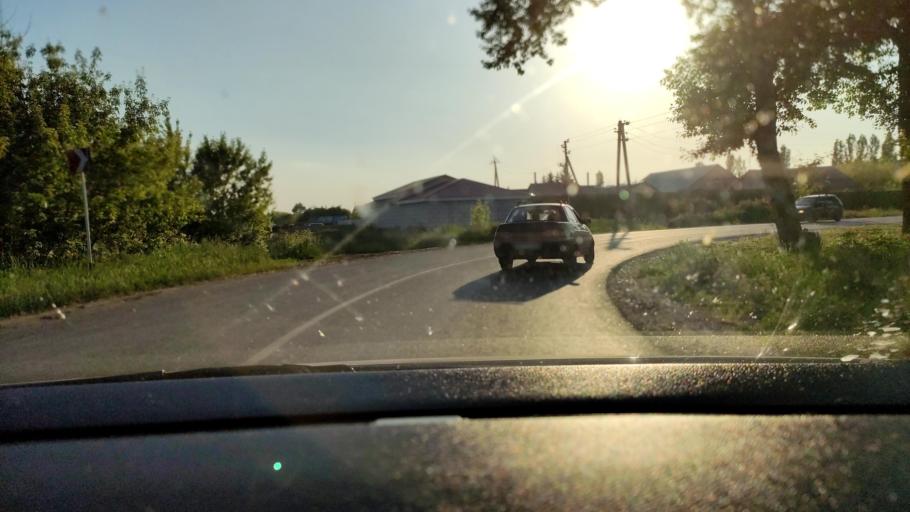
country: RU
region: Voronezj
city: Maslovka
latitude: 51.5363
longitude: 39.3434
